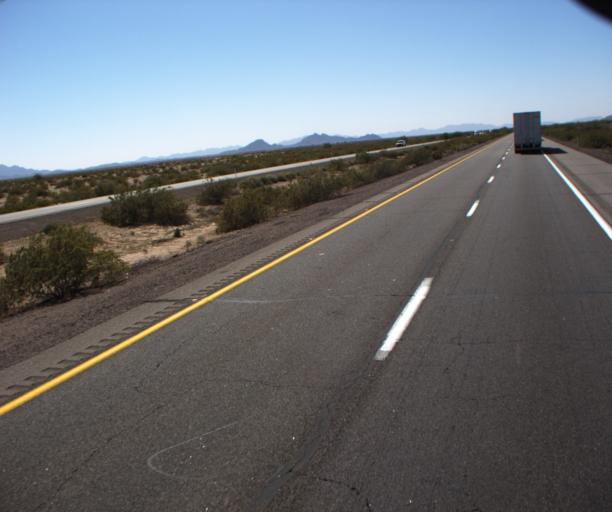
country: US
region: Arizona
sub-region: Yuma County
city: Wellton
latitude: 32.7081
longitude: -113.8584
